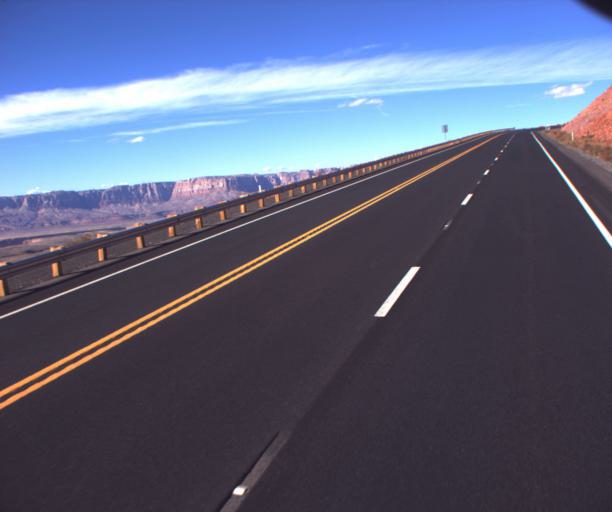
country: US
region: Arizona
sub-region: Coconino County
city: LeChee
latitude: 36.6535
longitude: -111.6323
